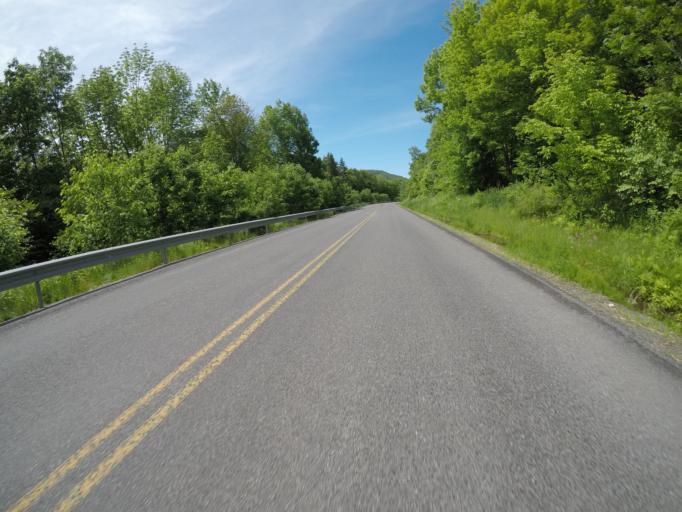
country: US
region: New York
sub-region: Sullivan County
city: Livingston Manor
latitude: 42.0938
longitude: -74.8233
